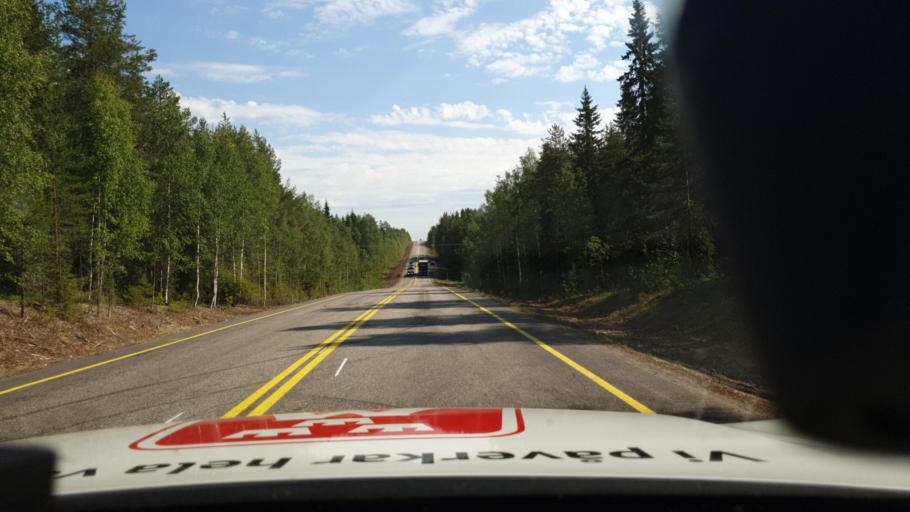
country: SE
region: Norrbotten
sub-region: Lulea Kommun
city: Ranea
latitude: 65.8648
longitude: 22.3122
